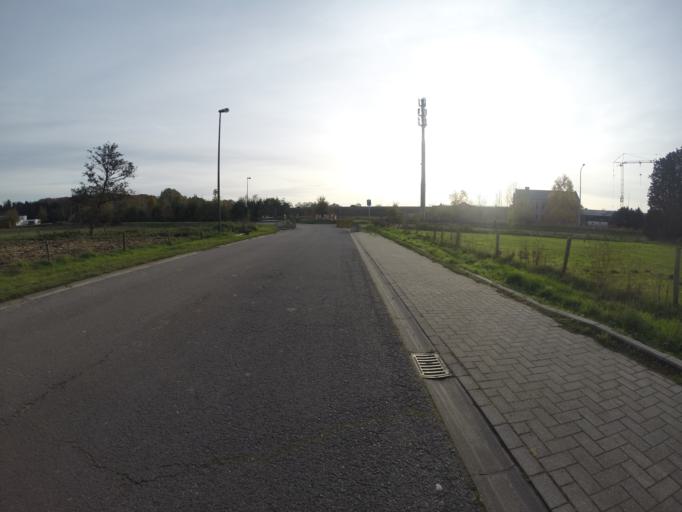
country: BE
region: Flanders
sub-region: Provincie Oost-Vlaanderen
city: Aalter
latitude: 51.0768
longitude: 3.4516
